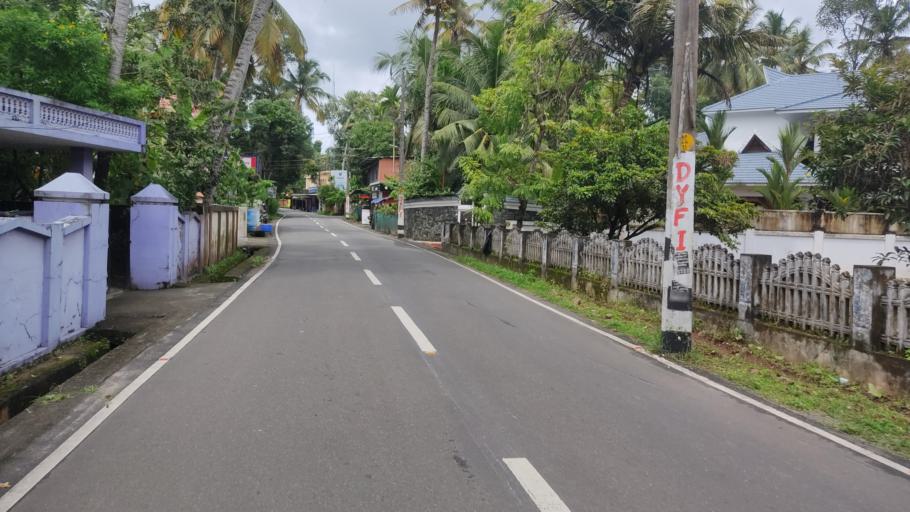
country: IN
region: Kerala
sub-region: Alappuzha
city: Kayankulam
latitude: 9.1648
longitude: 76.4918
